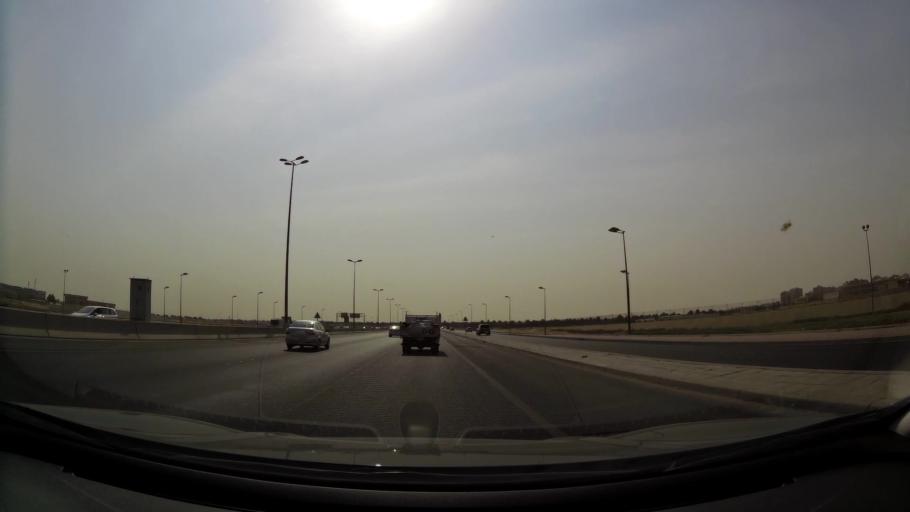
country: KW
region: Al Farwaniyah
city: Al Farwaniyah
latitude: 29.2641
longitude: 47.9522
